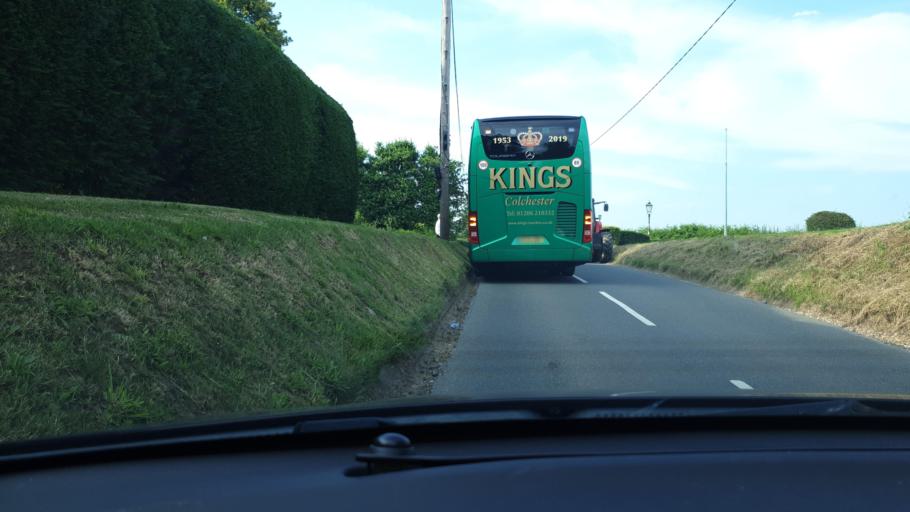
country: GB
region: England
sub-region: Essex
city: Little Clacton
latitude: 51.8635
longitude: 1.1203
